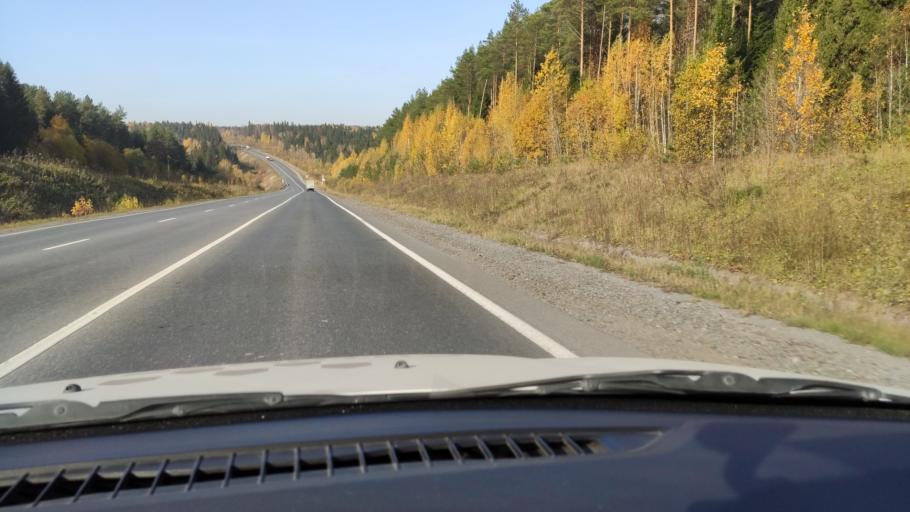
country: RU
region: Perm
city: Novyye Lyady
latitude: 58.0387
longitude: 56.4658
